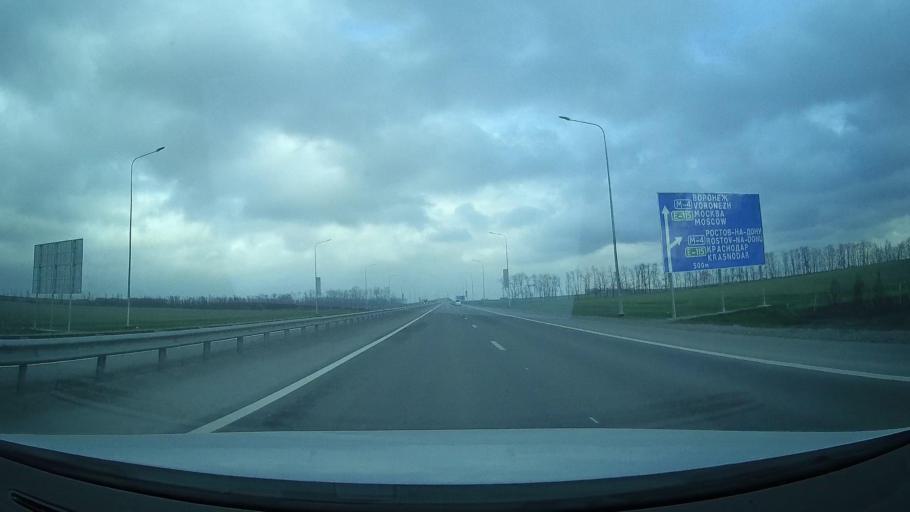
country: RU
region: Rostov
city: Grushevskaya
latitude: 47.4975
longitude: 39.9589
